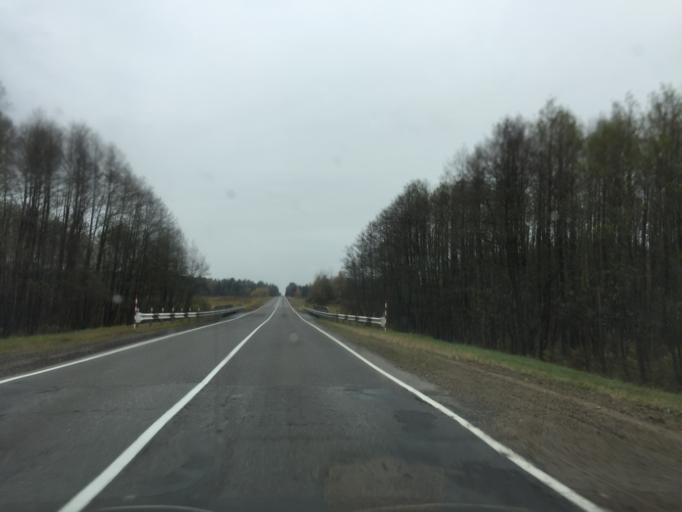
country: BY
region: Mogilev
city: Chavusy
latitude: 53.7317
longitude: 31.1165
